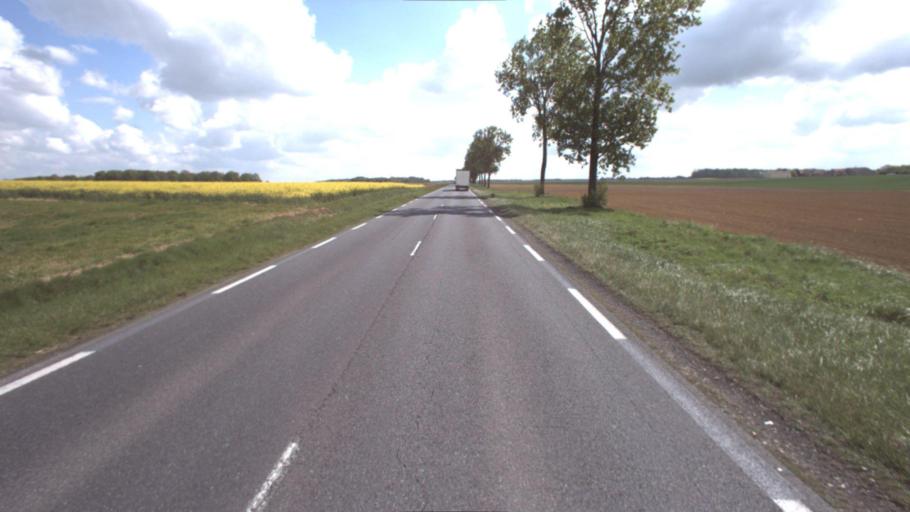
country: FR
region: Ile-de-France
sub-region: Departement de Seine-et-Marne
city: Jouy-le-Chatel
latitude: 48.6926
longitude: 3.1929
